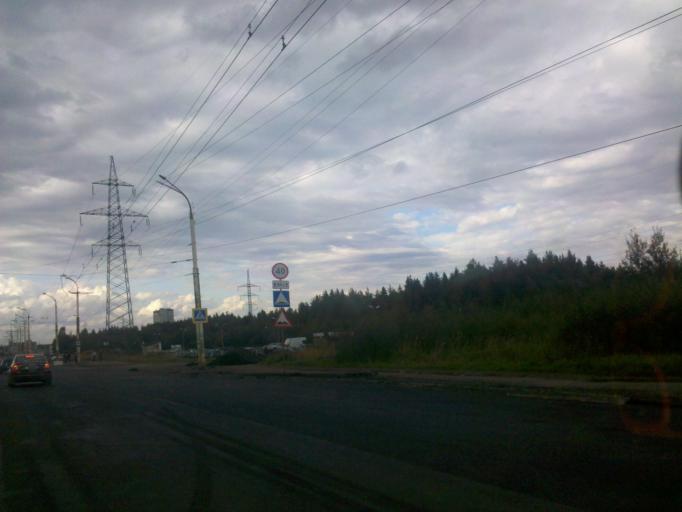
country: RU
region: Republic of Karelia
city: Petrozavodsk
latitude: 61.7731
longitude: 34.3147
